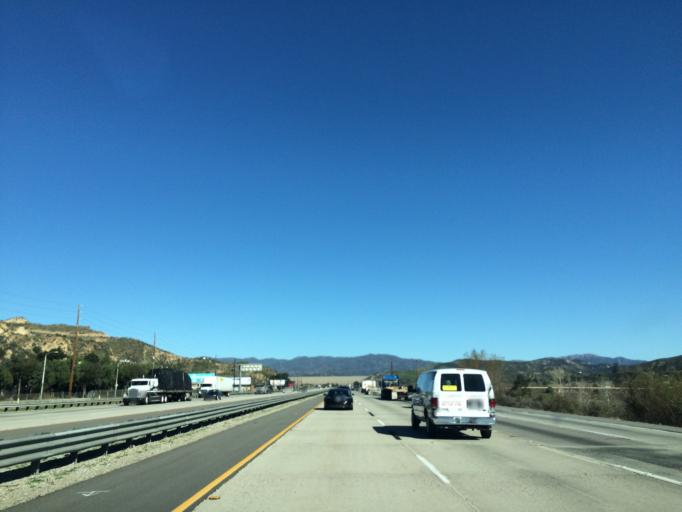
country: US
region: California
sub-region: Los Angeles County
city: Castaic
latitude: 34.4696
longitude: -118.6164
